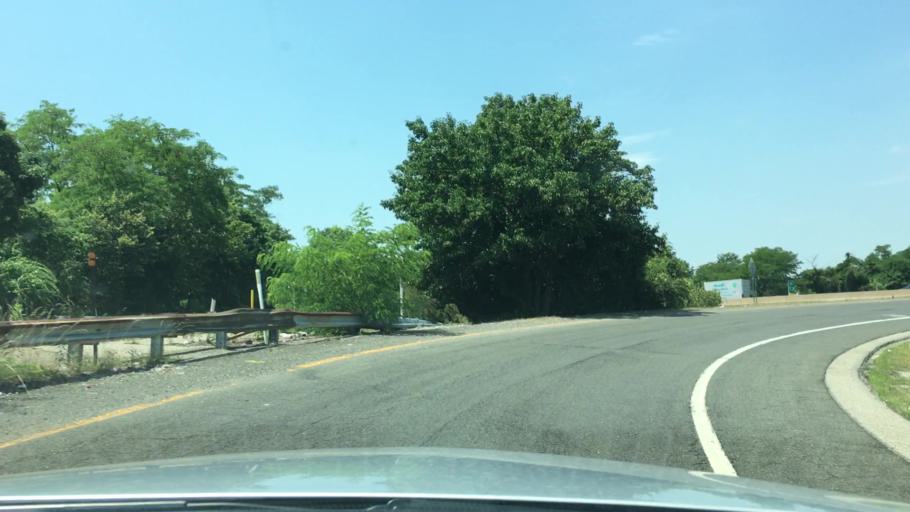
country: US
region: New York
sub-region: Nassau County
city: Plainedge
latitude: 40.7252
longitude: -73.4741
